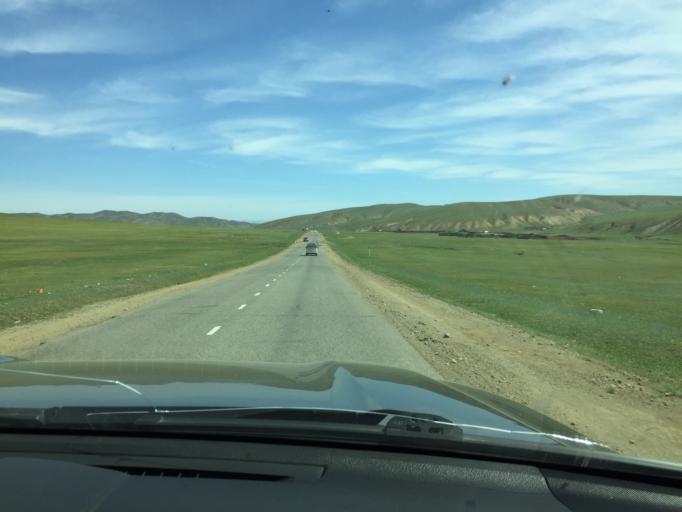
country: MN
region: Central Aimak
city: Bornuur
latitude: 48.6632
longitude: 106.1257
